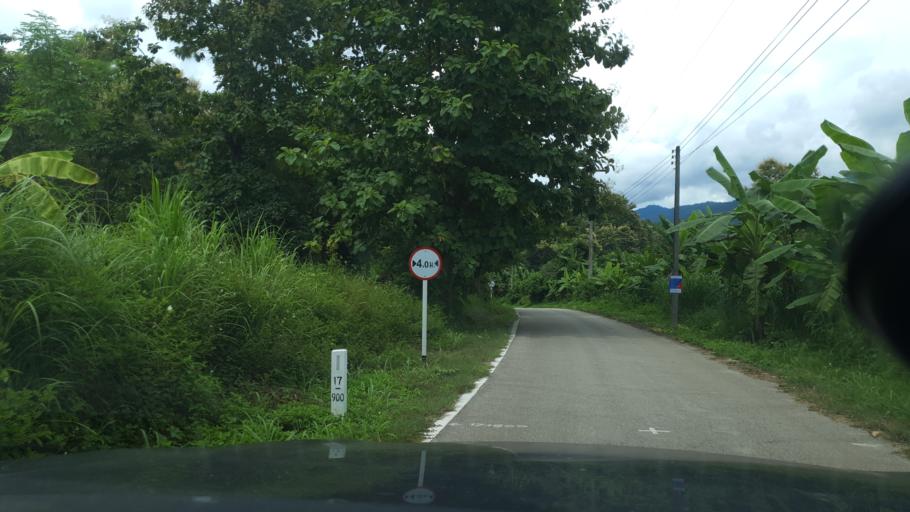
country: TH
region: Lampang
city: Hang Chat
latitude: 18.4248
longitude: 99.2649
